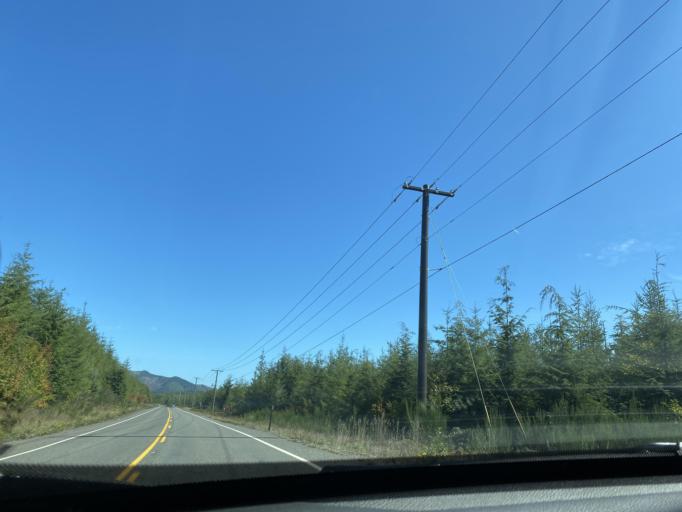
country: US
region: Washington
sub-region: Clallam County
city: Forks
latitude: 47.9626
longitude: -124.4261
